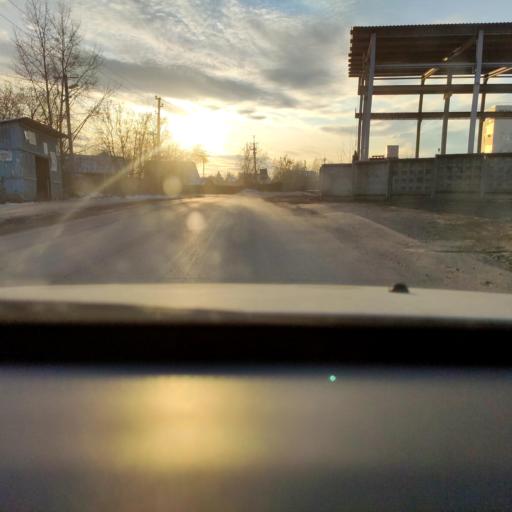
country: RU
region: Perm
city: Ferma
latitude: 57.9087
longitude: 56.3052
